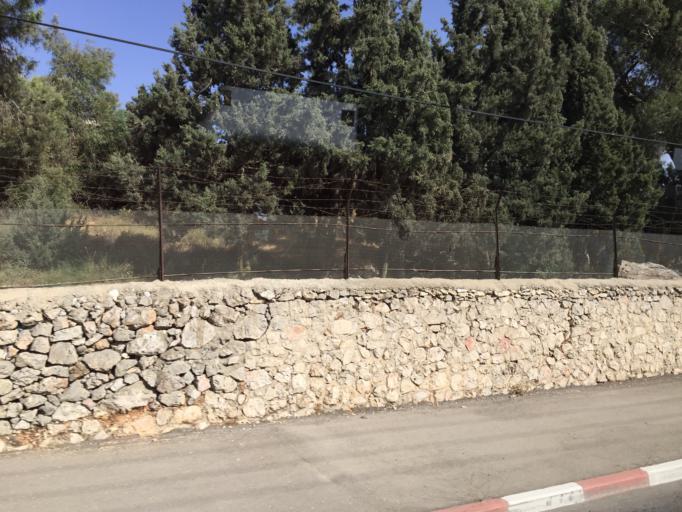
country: PS
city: Ad Dawhah
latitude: 31.7081
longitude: 35.1723
